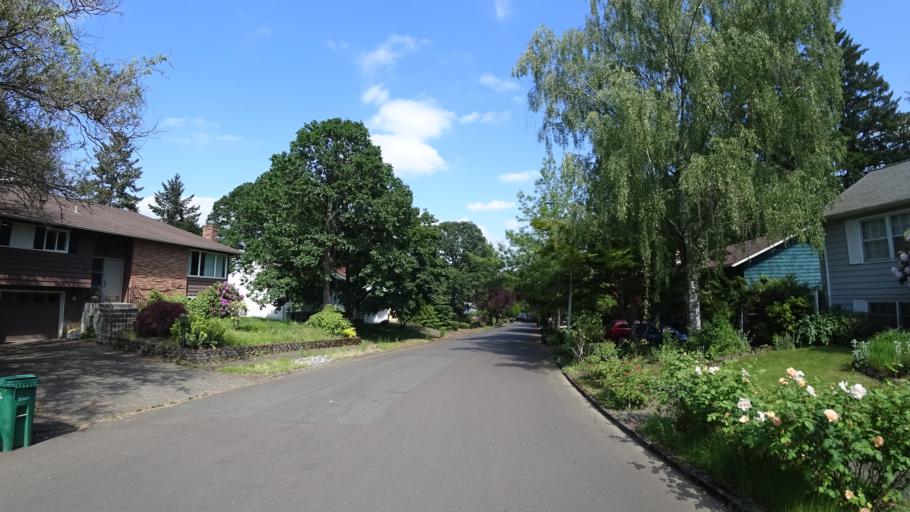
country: US
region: Oregon
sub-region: Washington County
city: Beaverton
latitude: 45.4650
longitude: -122.7947
